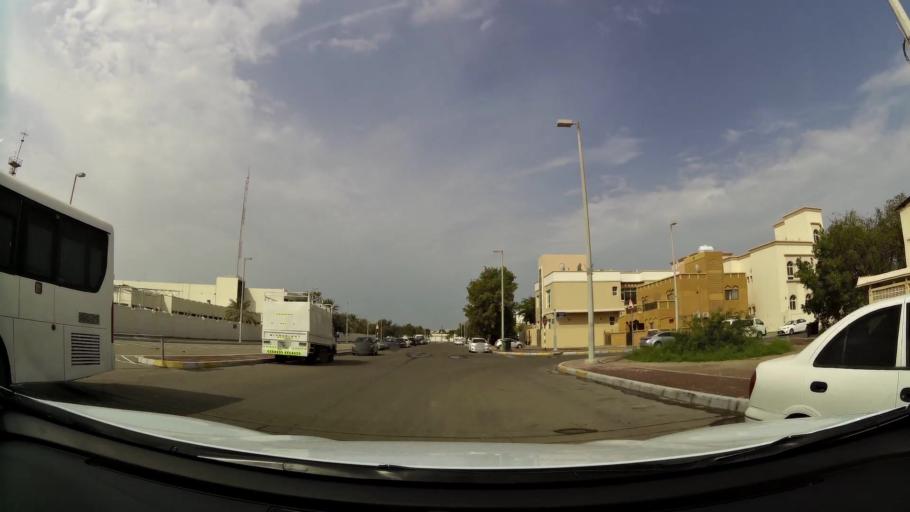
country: AE
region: Abu Dhabi
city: Abu Dhabi
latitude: 24.4397
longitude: 54.4301
